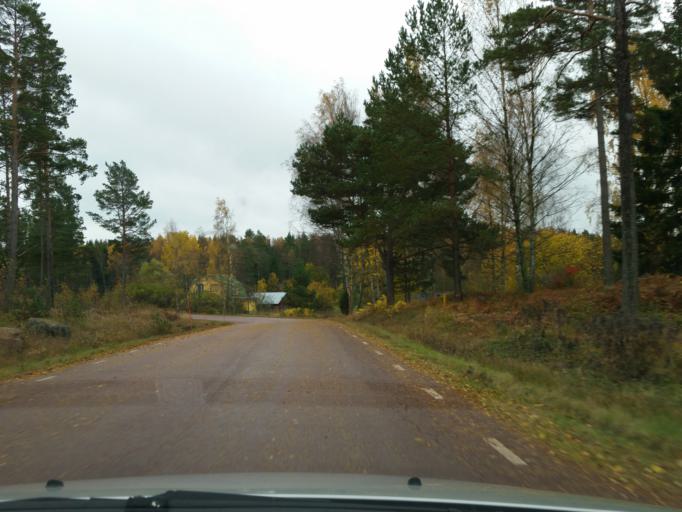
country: AX
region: Alands landsbygd
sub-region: Lumparland
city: Lumparland
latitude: 60.1317
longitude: 20.2739
